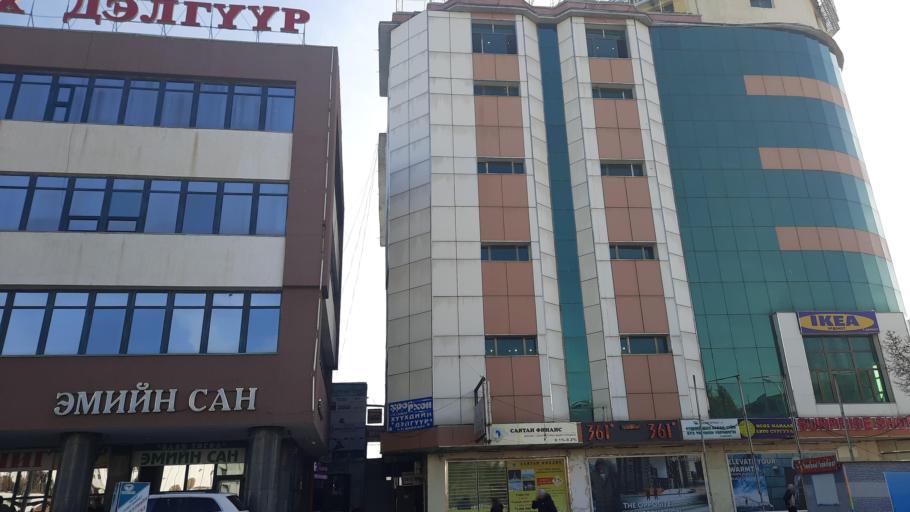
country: MN
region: Orhon
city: Erdenet
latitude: 49.0277
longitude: 104.0457
